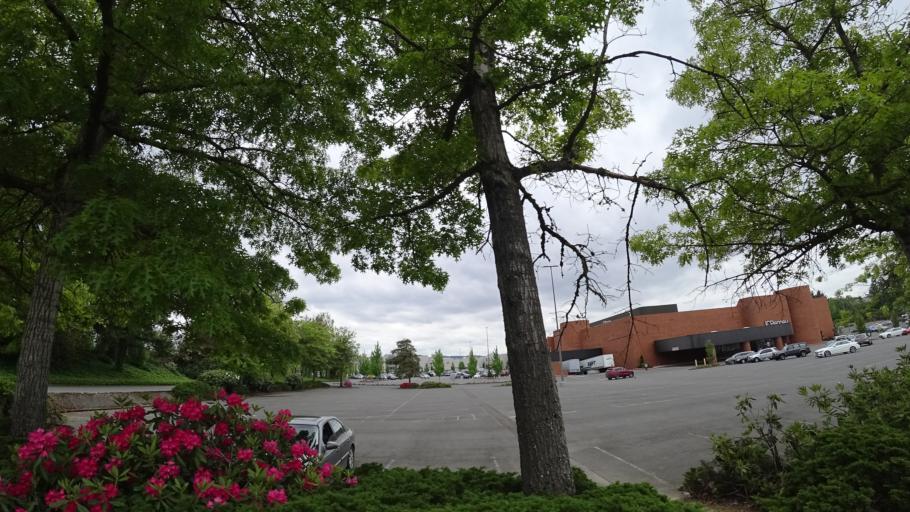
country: US
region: Oregon
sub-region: Washington County
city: Metzger
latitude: 45.4507
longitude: -122.7765
